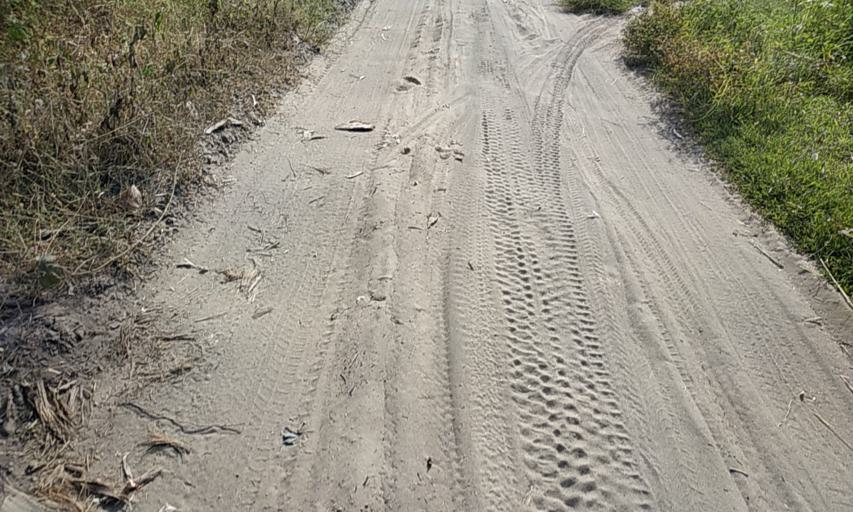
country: ID
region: Central Java
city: Gombong
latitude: -7.7619
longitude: 109.5136
